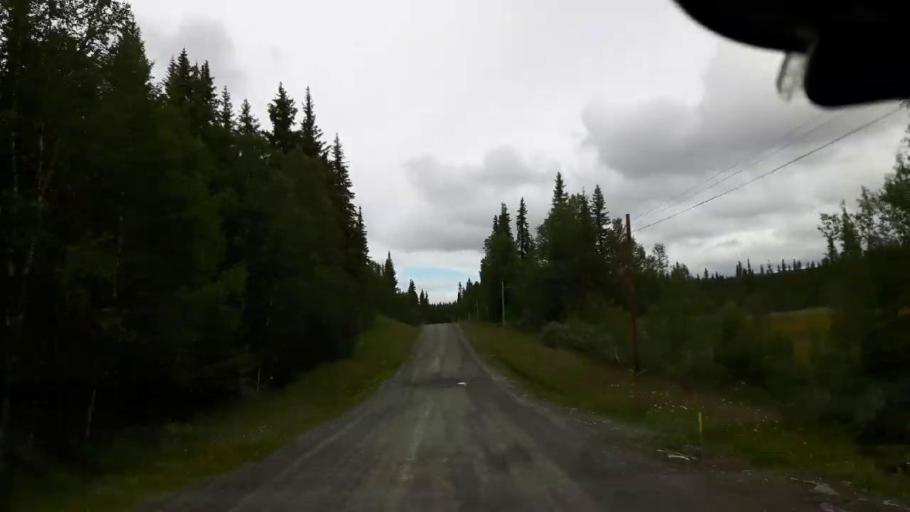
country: SE
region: Jaemtland
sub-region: Krokoms Kommun
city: Valla
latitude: 63.7428
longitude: 13.8368
